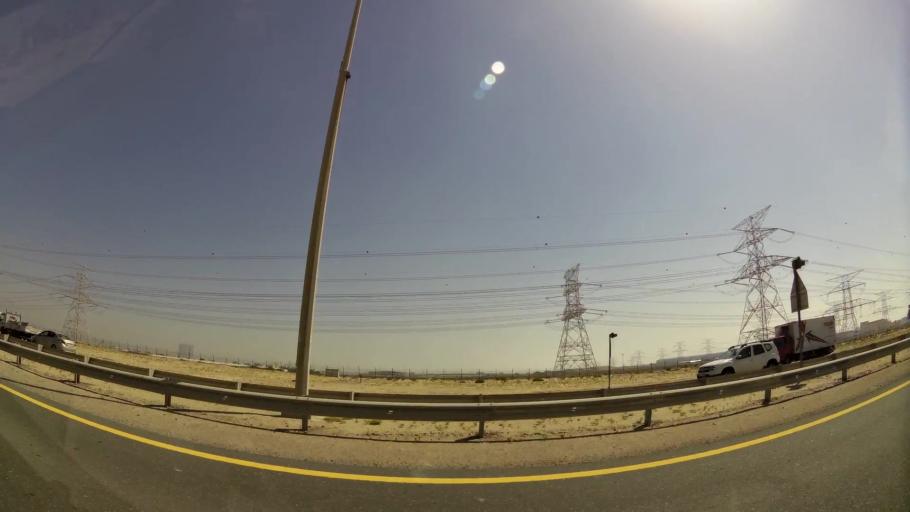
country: AE
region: Dubai
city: Dubai
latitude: 24.9345
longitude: 55.0801
